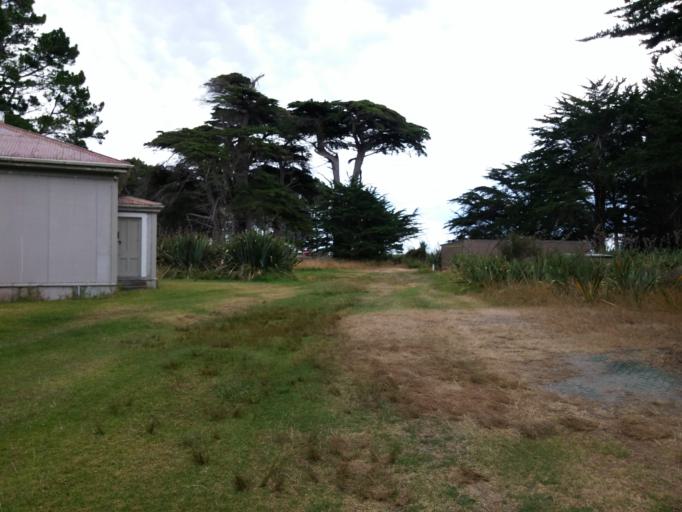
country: NZ
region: Tasman
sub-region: Tasman District
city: Takaka
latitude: -40.5462
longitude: 173.0080
